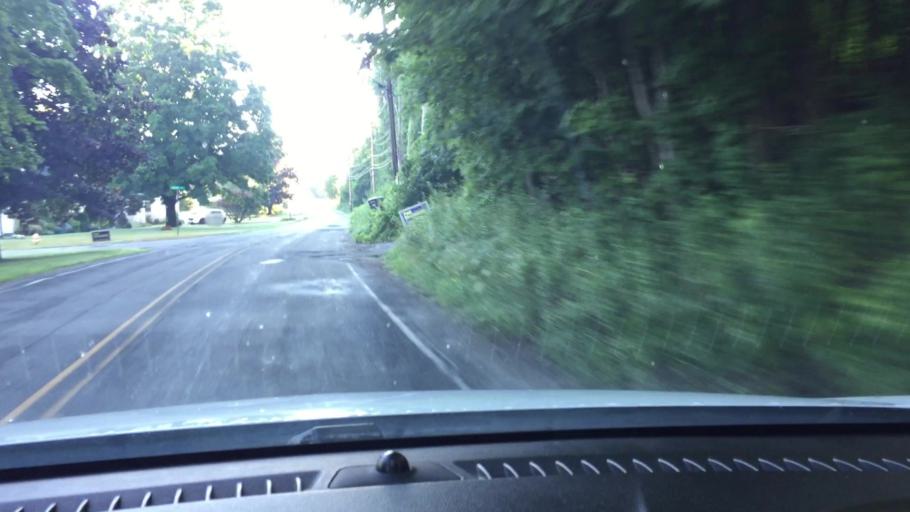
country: US
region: Massachusetts
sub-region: Berkshire County
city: Pittsfield
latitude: 42.4146
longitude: -73.2301
